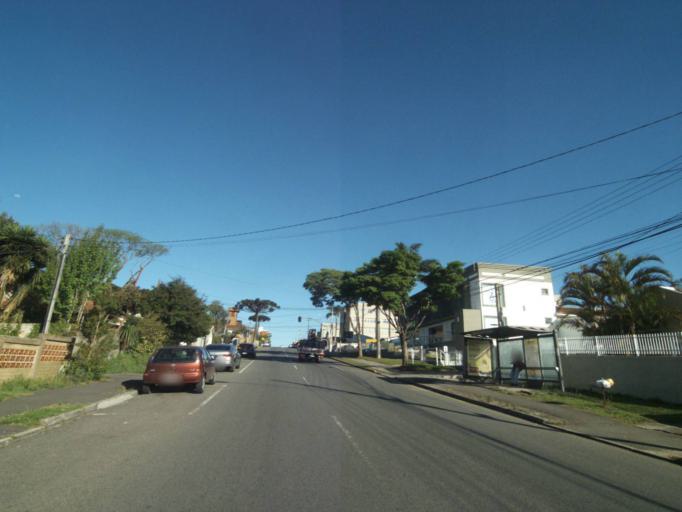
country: BR
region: Parana
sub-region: Curitiba
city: Curitiba
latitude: -25.3971
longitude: -49.2513
